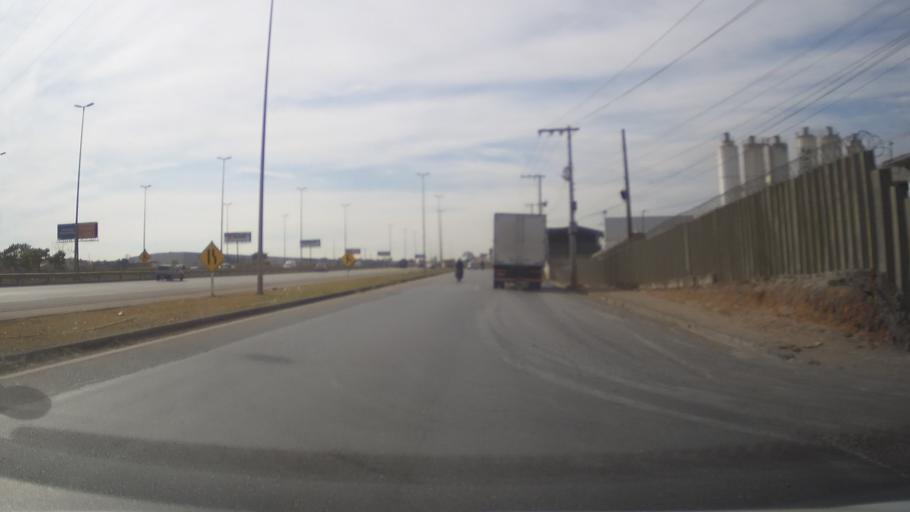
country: BR
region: Minas Gerais
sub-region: Contagem
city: Contagem
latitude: -19.9092
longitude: -44.0456
